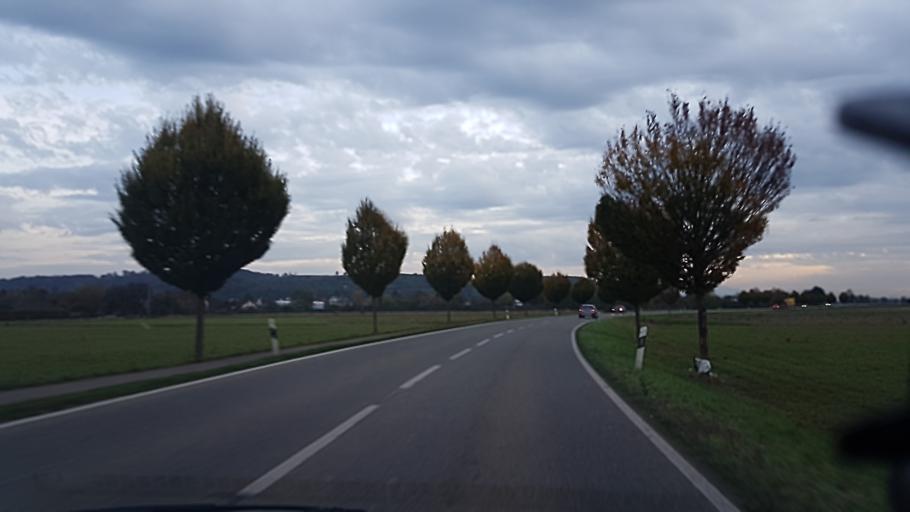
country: DE
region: Baden-Wuerttemberg
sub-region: Freiburg Region
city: Kenzingen
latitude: 48.1924
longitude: 7.7599
